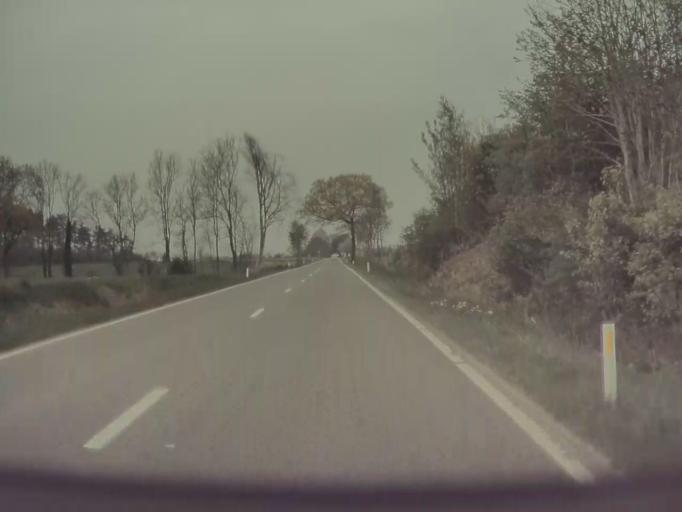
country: BE
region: Wallonia
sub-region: Province de Liege
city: Ferrieres
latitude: 50.4178
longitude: 5.5793
